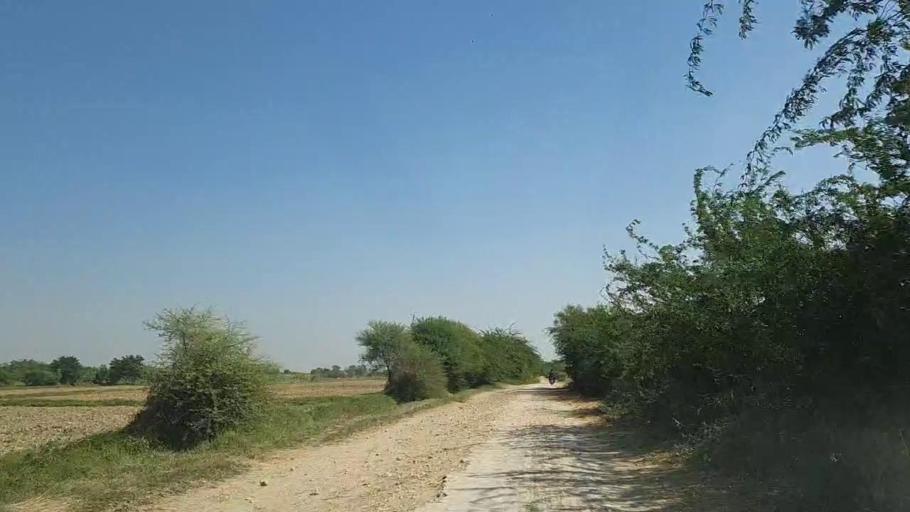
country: PK
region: Sindh
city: Mirpur Batoro
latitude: 24.7313
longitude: 68.2168
